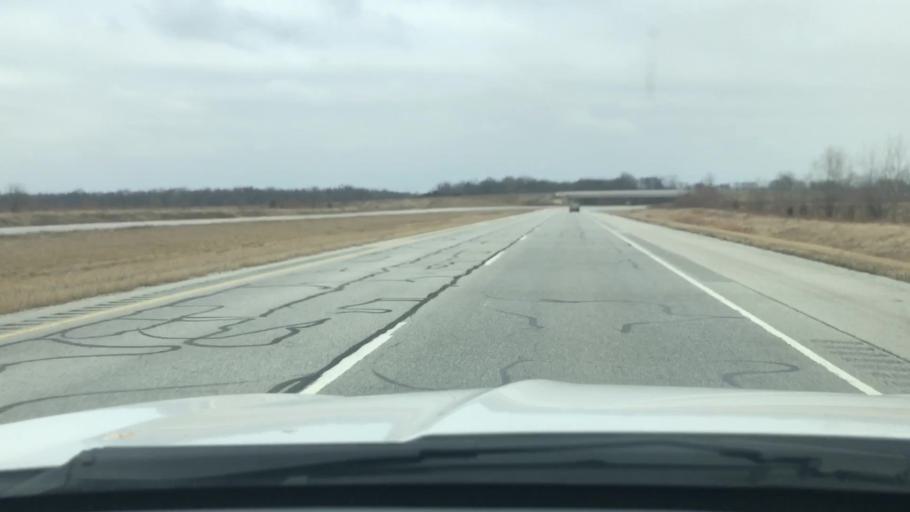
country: US
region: Indiana
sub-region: Carroll County
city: Delphi
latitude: 40.6415
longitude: -86.5808
